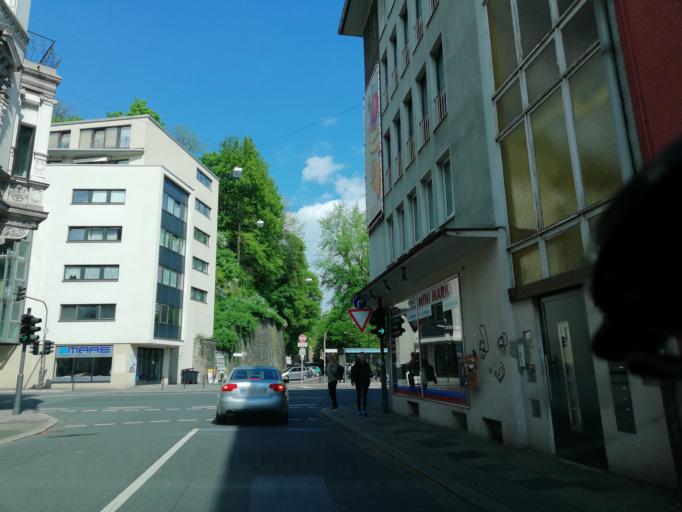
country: DE
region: North Rhine-Westphalia
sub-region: Regierungsbezirk Dusseldorf
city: Wuppertal
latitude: 51.2541
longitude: 7.1317
